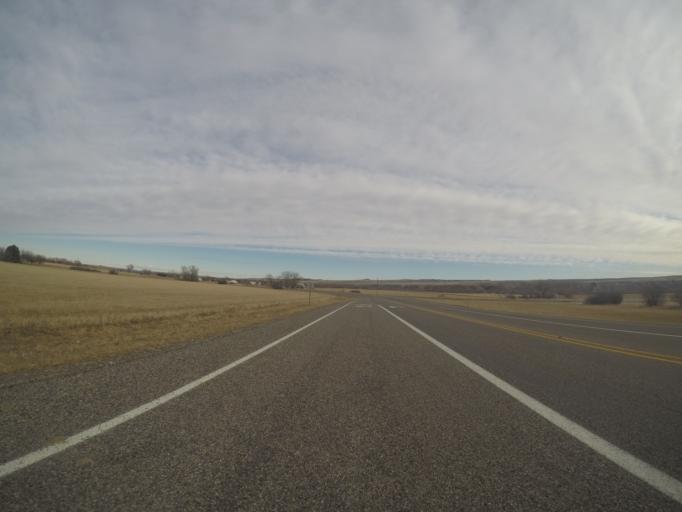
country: US
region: Montana
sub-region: Yellowstone County
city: Laurel
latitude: 45.5383
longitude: -108.8505
